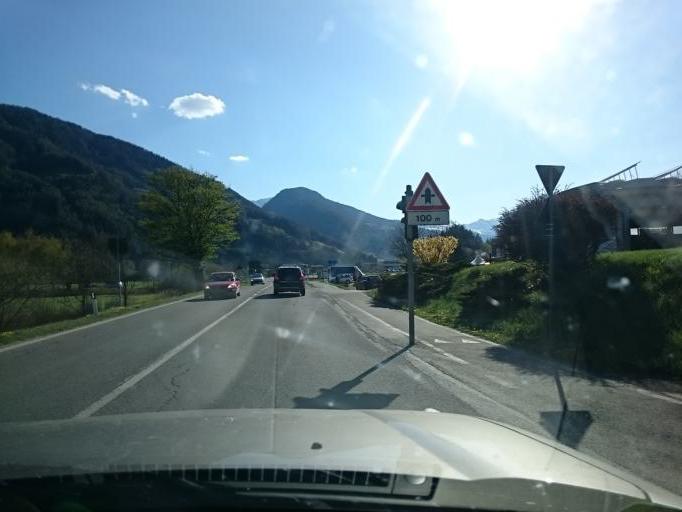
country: IT
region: Trentino-Alto Adige
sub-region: Bolzano
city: Vipiteno
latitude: 46.8904
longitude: 11.4357
